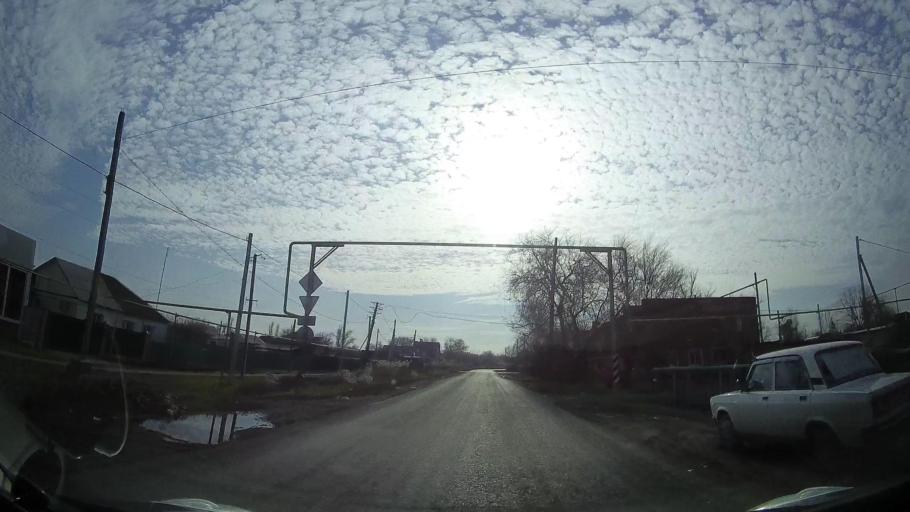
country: RU
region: Rostov
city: Veselyy
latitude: 47.0906
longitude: 40.7417
